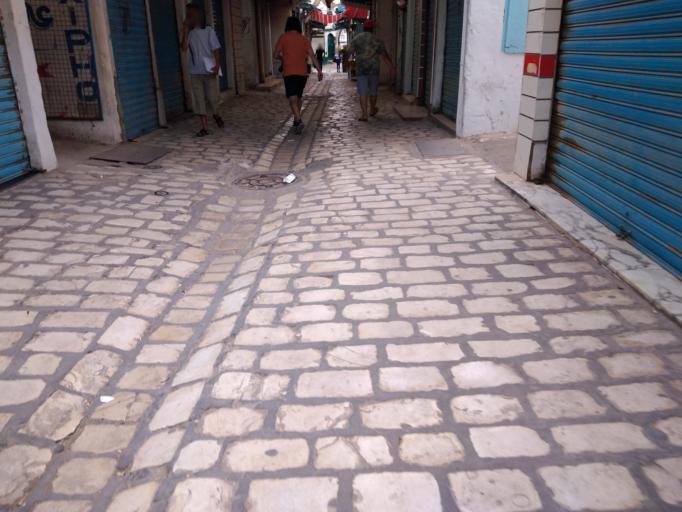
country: TN
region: Safaqis
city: Sfax
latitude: 34.7372
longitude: 10.7606
